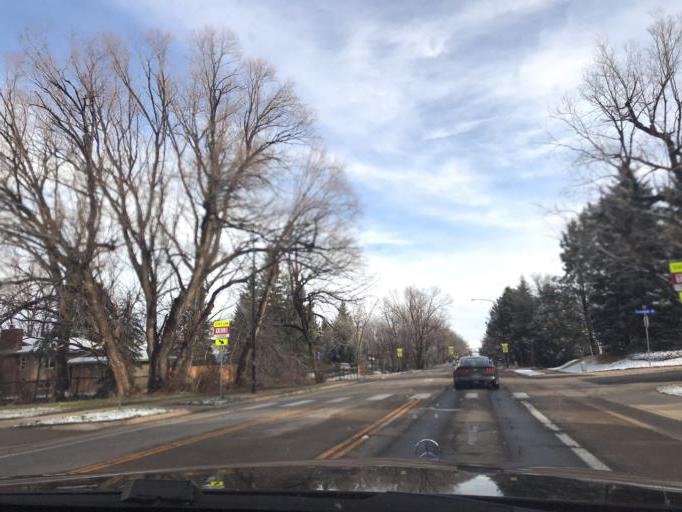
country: US
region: Colorado
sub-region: Boulder County
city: Boulder
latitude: 40.0010
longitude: -105.2253
